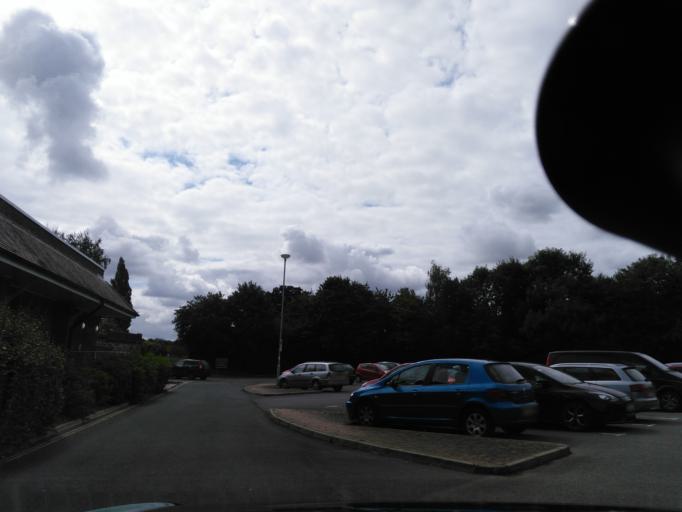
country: GB
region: England
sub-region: Dorset
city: Blandford Forum
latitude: 50.8559
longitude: -2.1598
